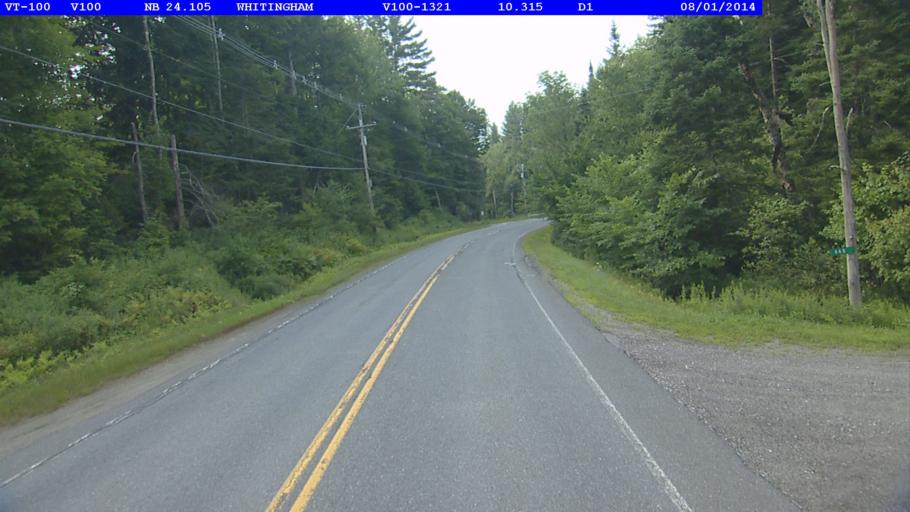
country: US
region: Vermont
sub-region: Windham County
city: Dover
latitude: 42.8228
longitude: -72.8582
